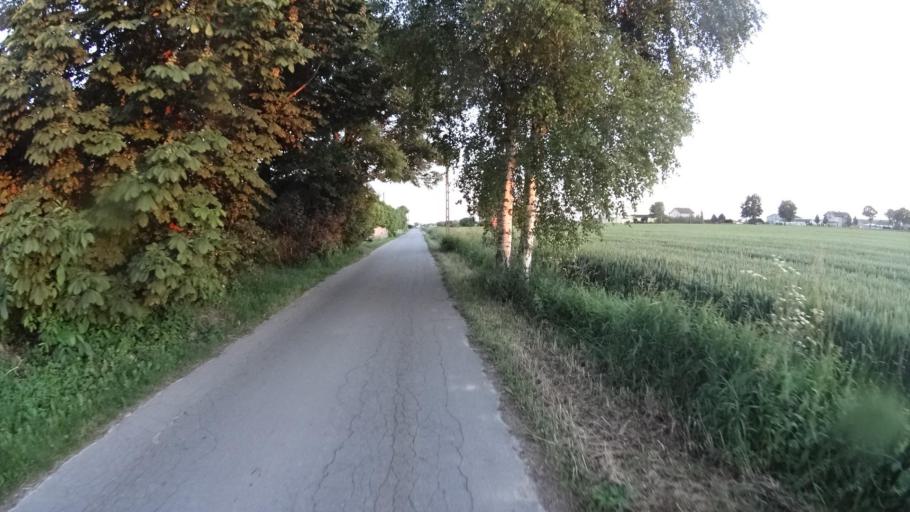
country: PL
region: Masovian Voivodeship
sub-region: Powiat warszawski zachodni
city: Blonie
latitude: 52.2388
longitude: 20.6582
